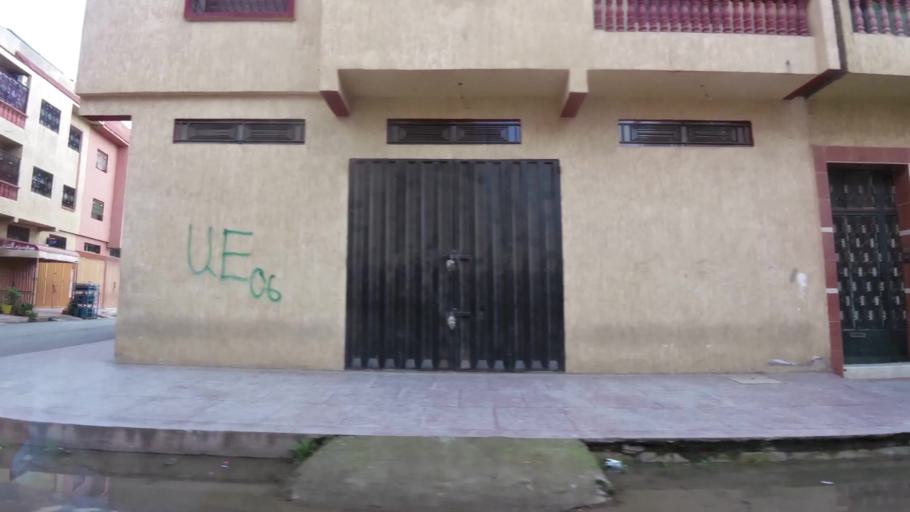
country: MA
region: Chaouia-Ouardigha
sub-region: Settat Province
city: Berrechid
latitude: 33.2671
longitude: -7.5723
